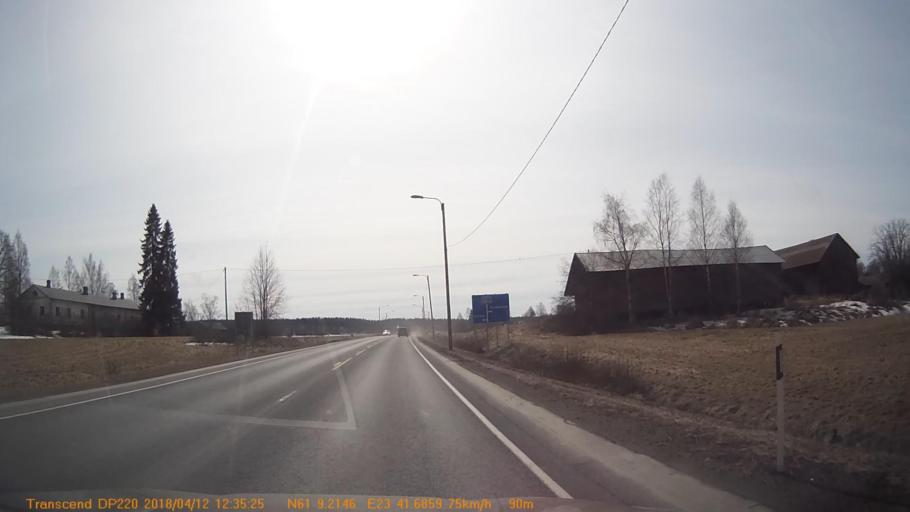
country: FI
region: Pirkanmaa
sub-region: Etelae-Pirkanmaa
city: Kylmaekoski
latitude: 61.1537
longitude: 23.6948
